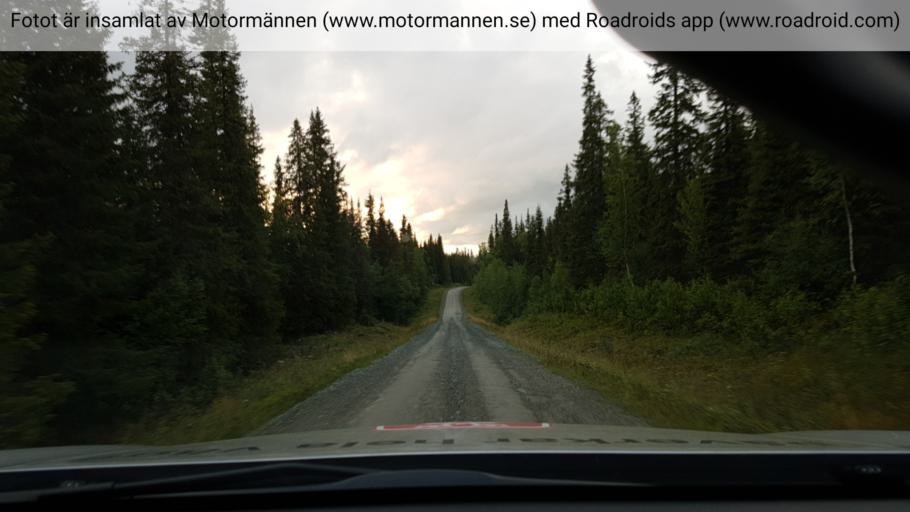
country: SE
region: Vaesterbotten
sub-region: Vilhelmina Kommun
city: Sjoberg
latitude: 65.5034
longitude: 15.4790
